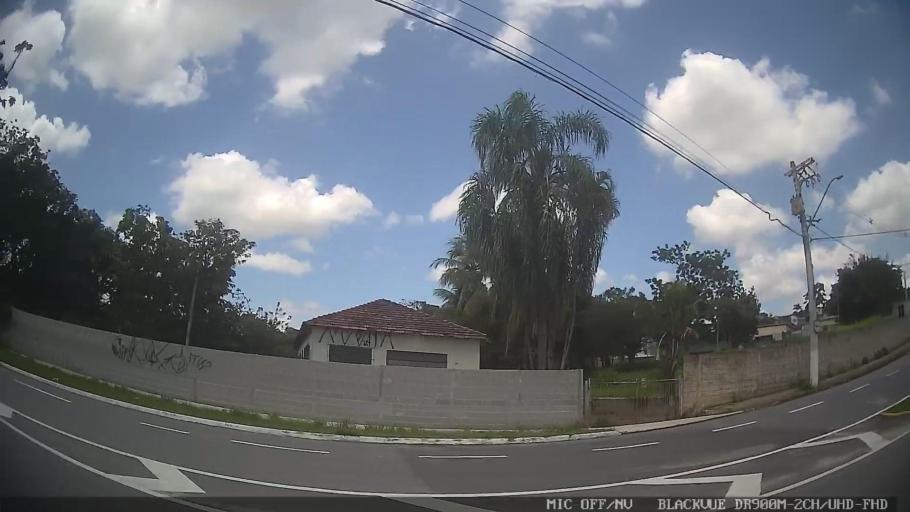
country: BR
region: Sao Paulo
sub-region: Jacarei
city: Jacarei
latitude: -23.3112
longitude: -45.9974
